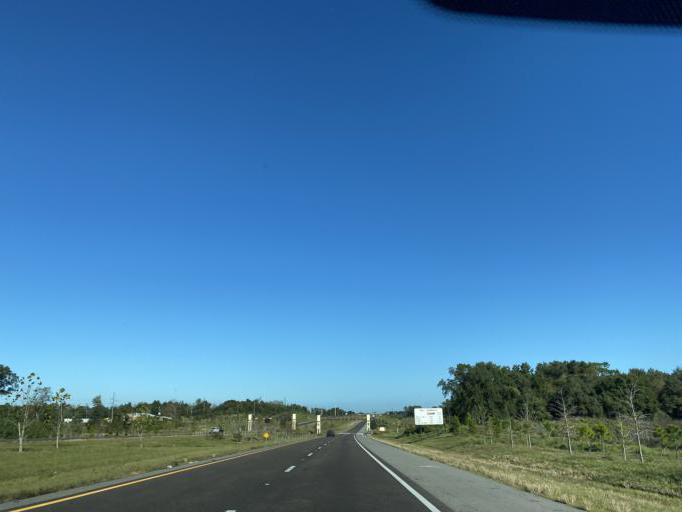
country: US
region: Florida
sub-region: Orange County
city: Zellwood
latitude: 28.7189
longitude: -81.5623
